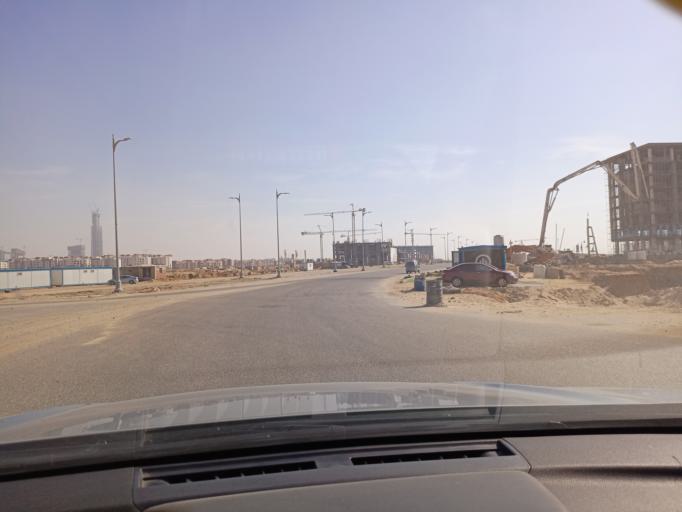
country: EG
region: Muhafazat al Qalyubiyah
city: Al Khankah
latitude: 30.0379
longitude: 31.6830
